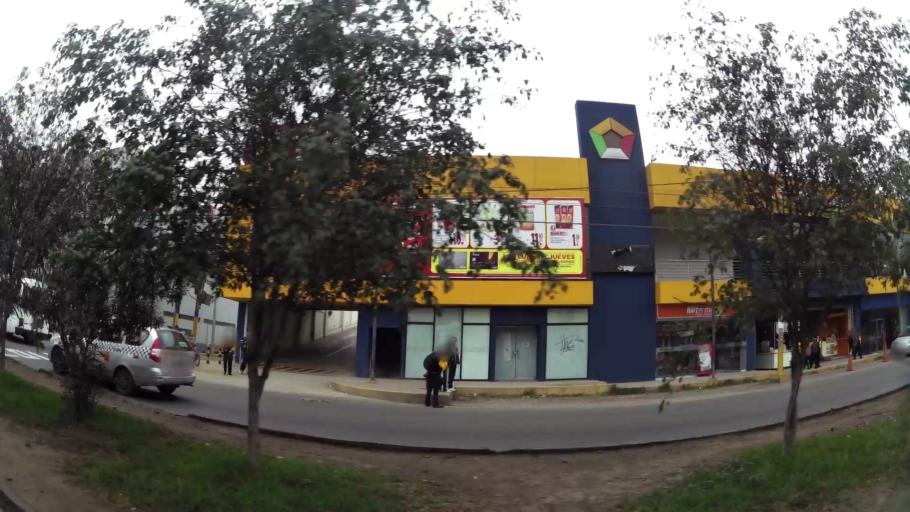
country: PE
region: Lima
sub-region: Lima
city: Independencia
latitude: -11.9787
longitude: -77.0111
